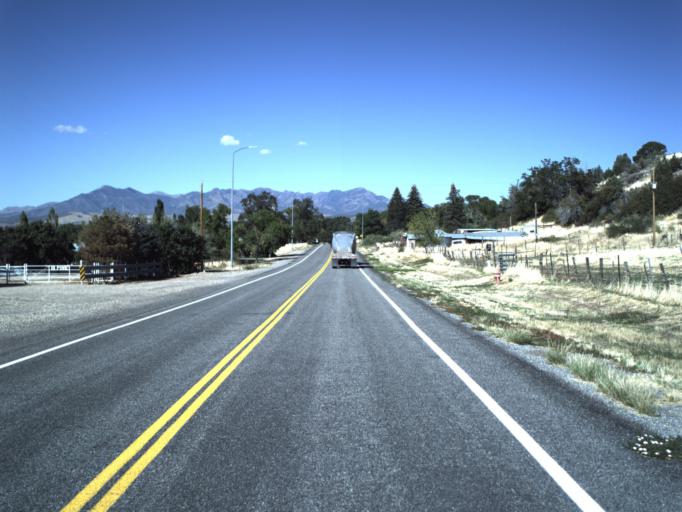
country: US
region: Utah
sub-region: Millard County
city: Fillmore
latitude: 39.0902
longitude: -112.2724
